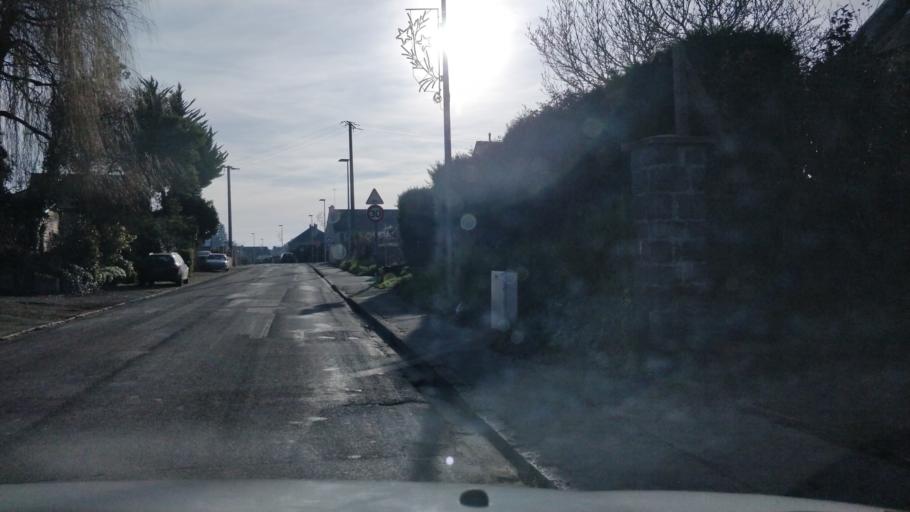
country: FR
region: Brittany
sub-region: Departement d'Ille-et-Vilaine
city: Plerguer
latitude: 48.5251
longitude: -1.8476
